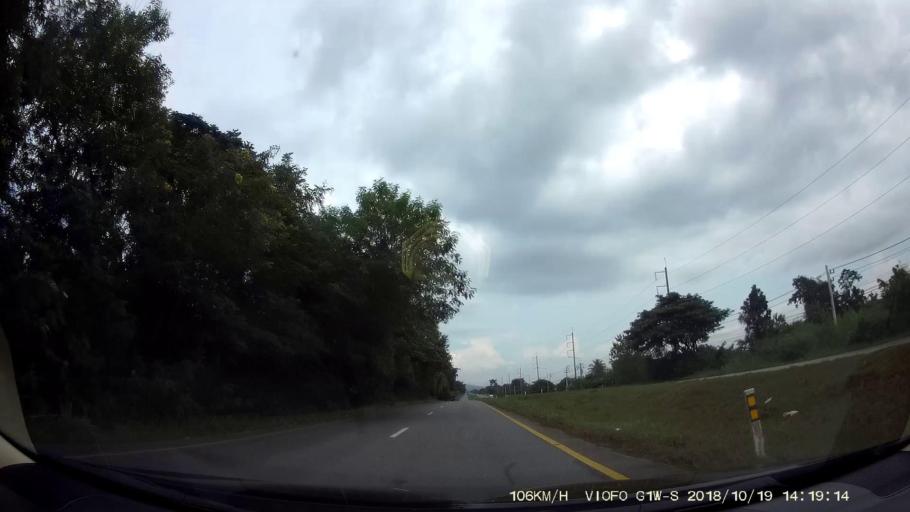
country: TH
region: Chaiyaphum
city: Kaeng Khro
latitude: 16.0254
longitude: 102.2434
